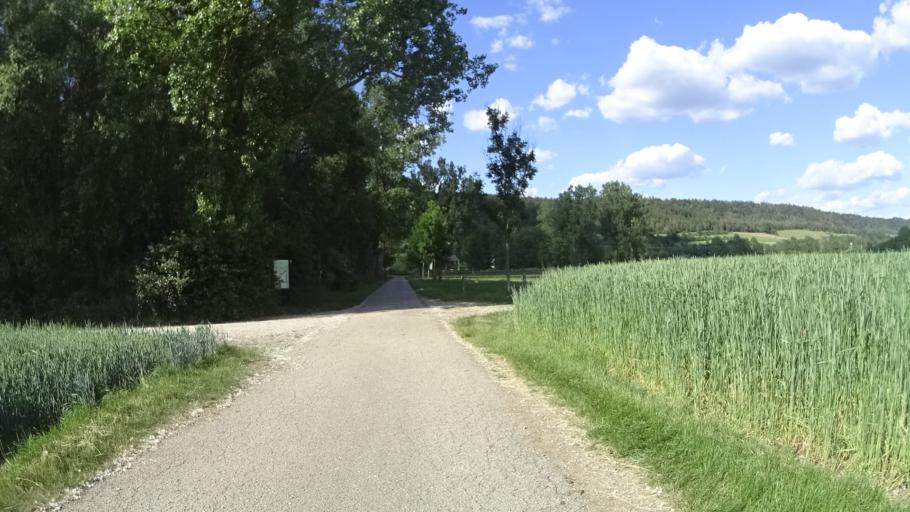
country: DE
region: Bavaria
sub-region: Upper Palatinate
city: Dietfurt
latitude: 49.0205
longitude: 11.4997
